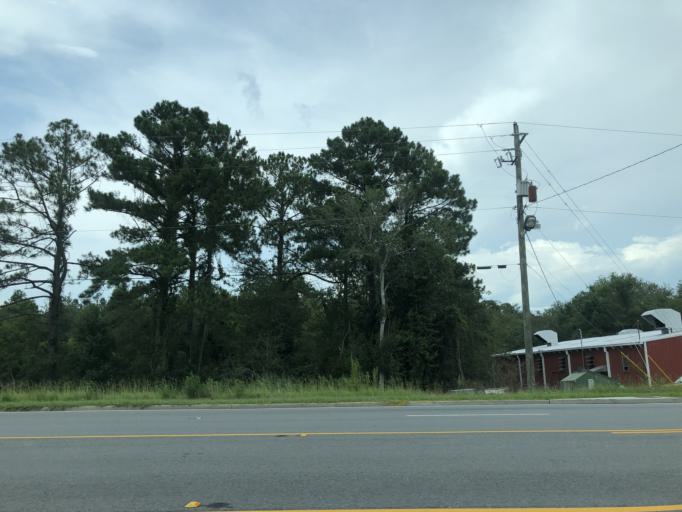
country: US
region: Georgia
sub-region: Wayne County
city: Jesup
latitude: 31.6164
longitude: -81.8924
